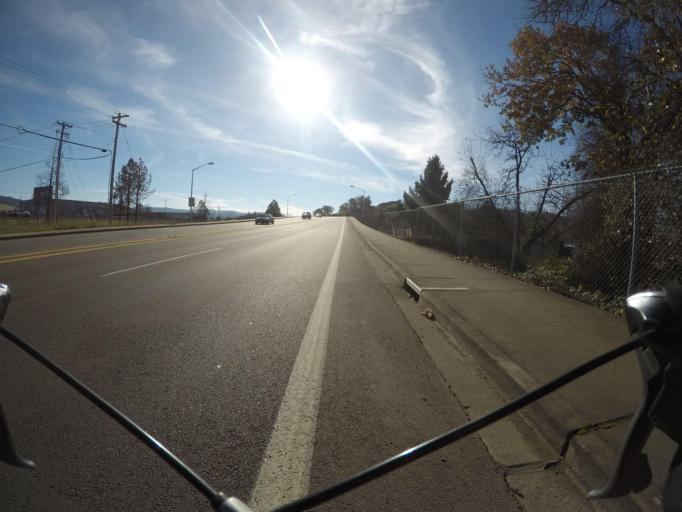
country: US
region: Oregon
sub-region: Douglas County
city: Roseburg
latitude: 43.2388
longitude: -123.3616
